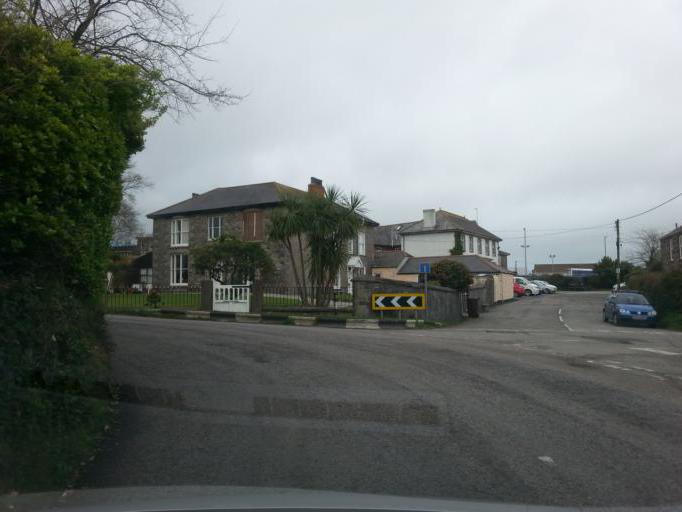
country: GB
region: England
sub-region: Cornwall
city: Camborne
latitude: 50.2205
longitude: -5.2673
